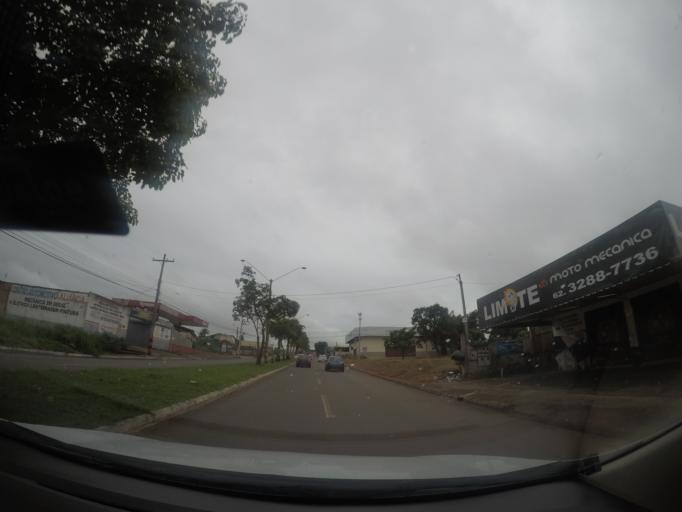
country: BR
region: Goias
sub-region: Aparecida De Goiania
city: Aparecida de Goiania
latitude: -16.7634
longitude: -49.3228
